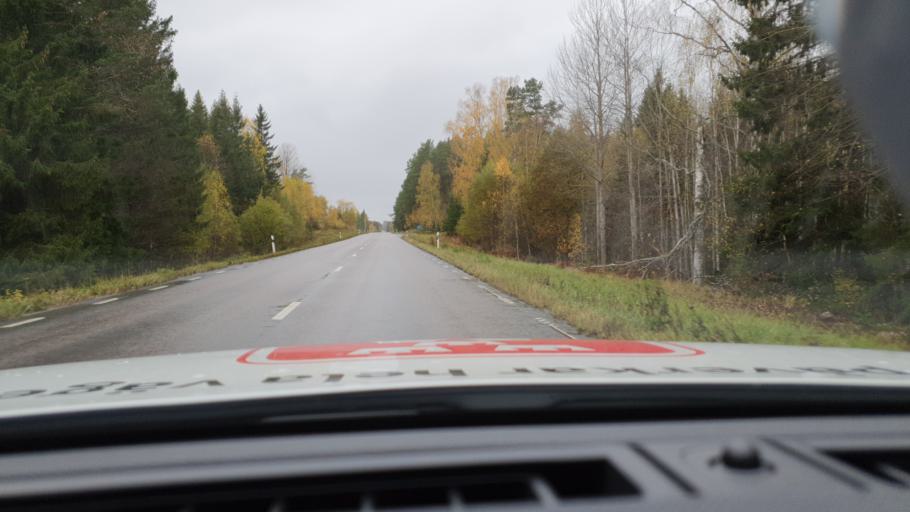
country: SE
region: Uppsala
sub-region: Tierps Kommun
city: Karlholmsbruk
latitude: 60.5347
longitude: 17.5767
